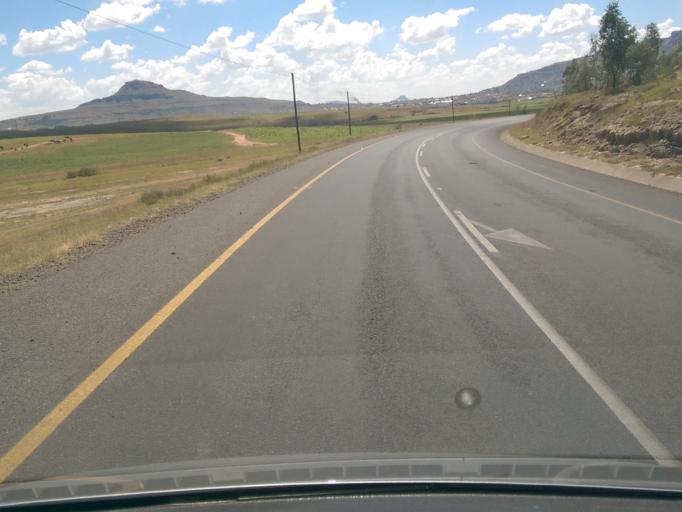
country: LS
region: Maseru
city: Maseru
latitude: -29.3937
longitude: 27.5056
